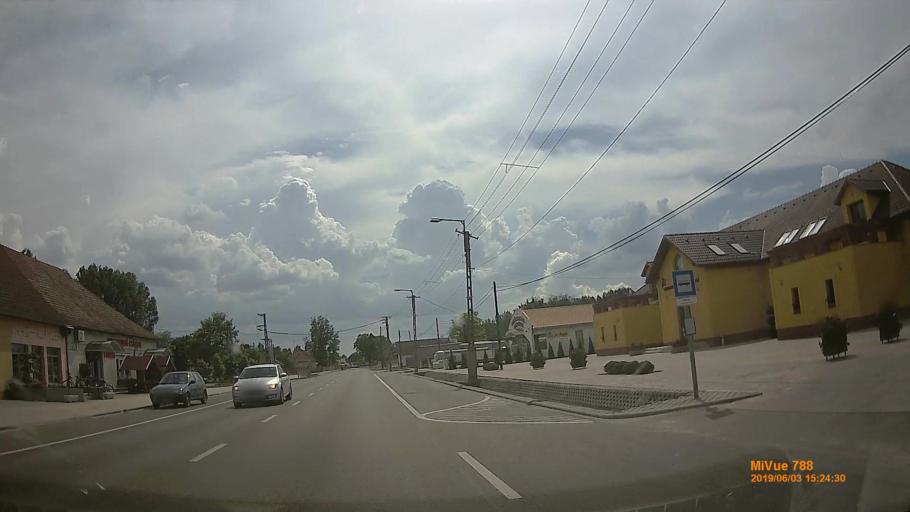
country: HU
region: Bacs-Kiskun
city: Tazlar
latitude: 46.6152
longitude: 19.4765
